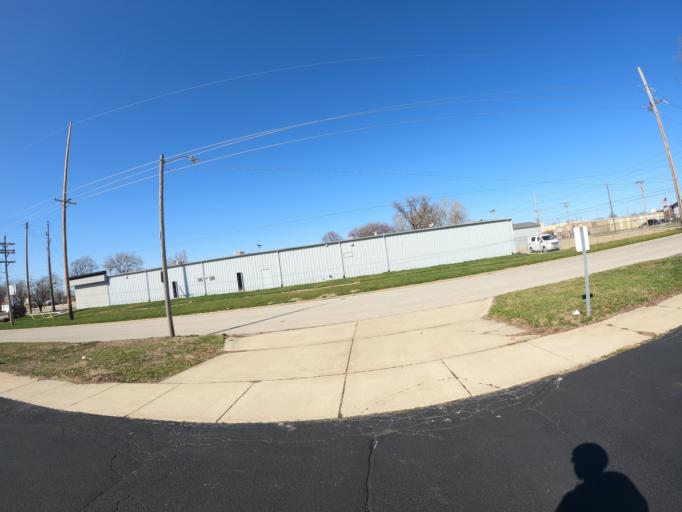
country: US
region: Illinois
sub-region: Sangamon County
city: Springfield
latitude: 39.8050
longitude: -89.6538
